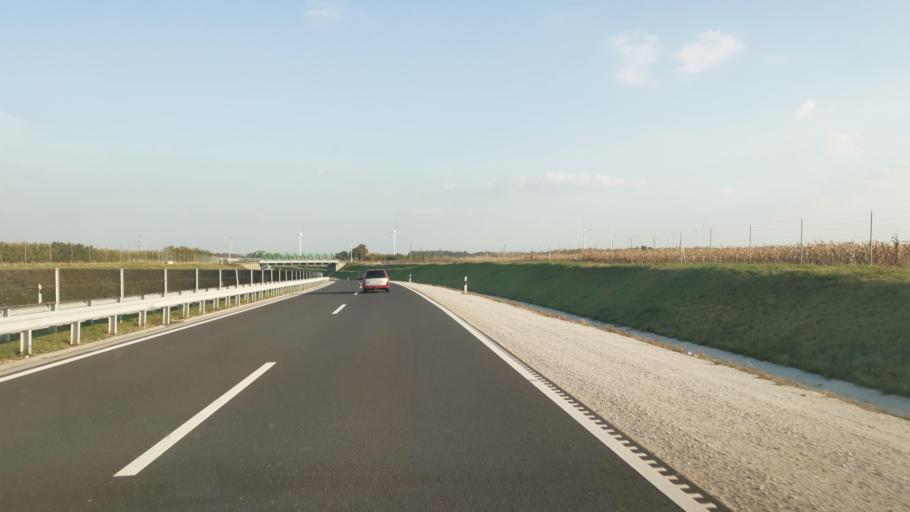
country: HU
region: Gyor-Moson-Sopron
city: Nagycenk
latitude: 47.5831
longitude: 16.7204
